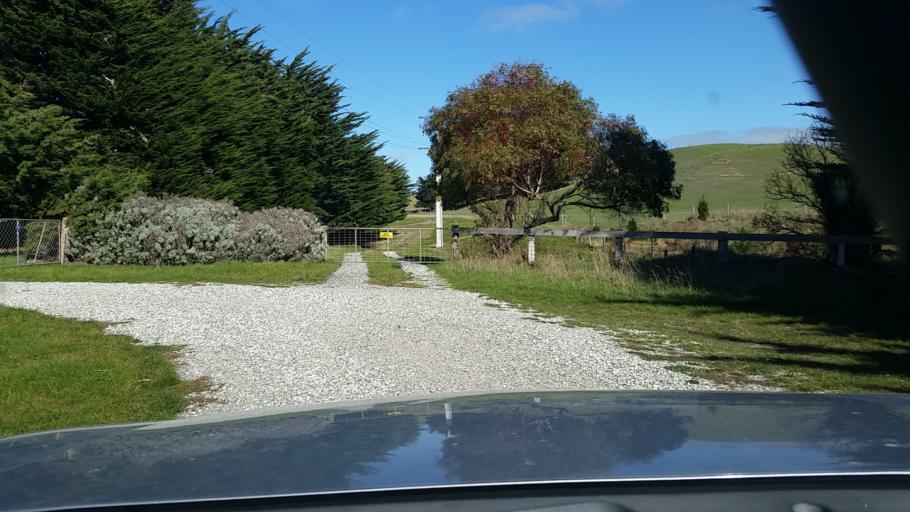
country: NZ
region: Marlborough
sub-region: Marlborough District
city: Blenheim
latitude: -41.7413
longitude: 174.1668
